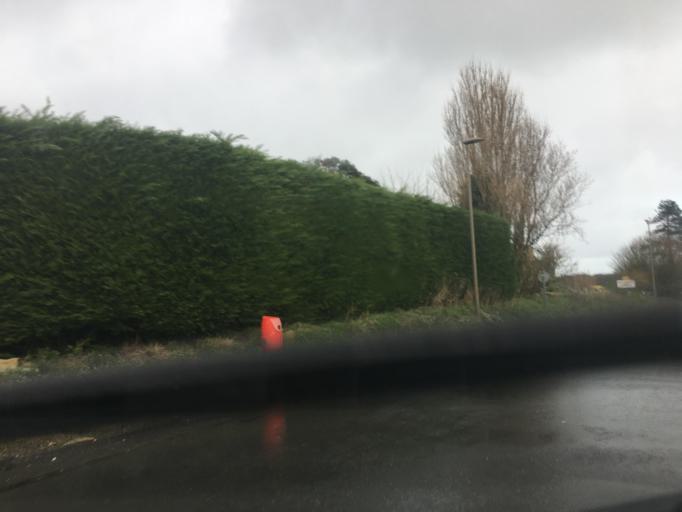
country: FR
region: Lower Normandy
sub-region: Departement de la Manche
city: Reville
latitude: 49.6886
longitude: -1.2821
